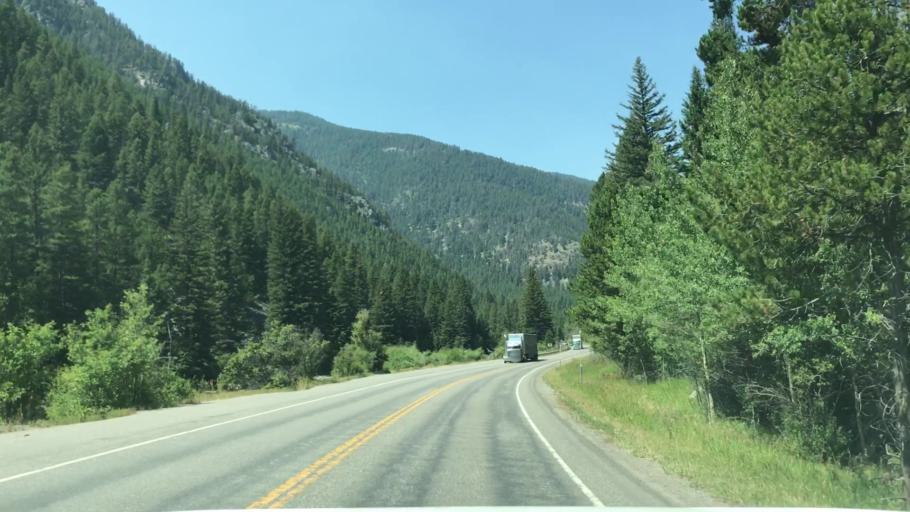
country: US
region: Montana
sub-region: Gallatin County
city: Big Sky
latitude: 45.3960
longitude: -111.2095
